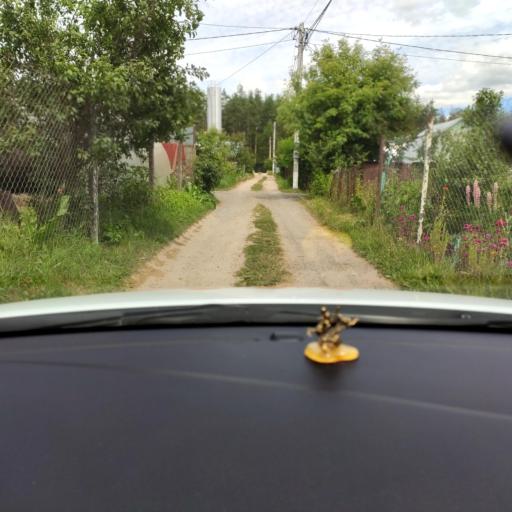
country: RU
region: Tatarstan
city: Staroye Arakchino
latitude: 55.8922
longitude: 49.0444
